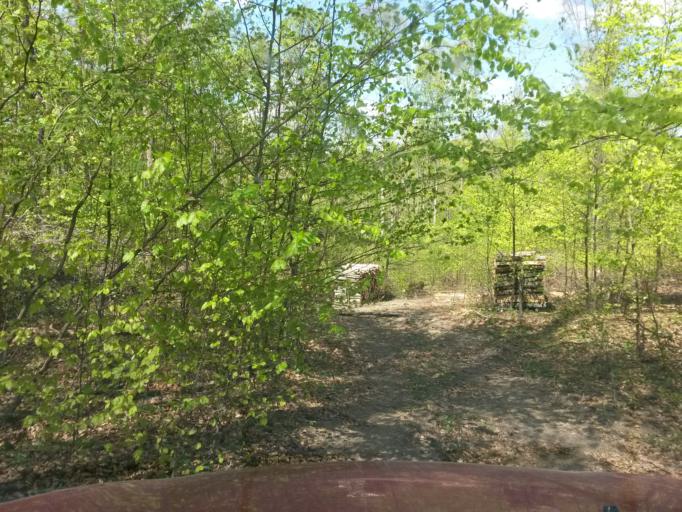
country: SK
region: Presovsky
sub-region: Okres Presov
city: Presov
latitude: 48.9438
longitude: 21.1336
